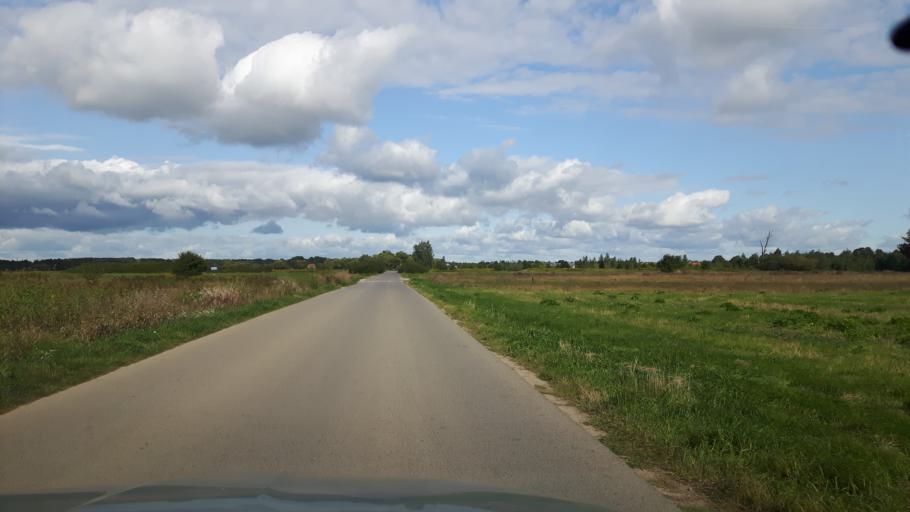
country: PL
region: Masovian Voivodeship
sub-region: Powiat wolominski
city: Marki
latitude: 52.3294
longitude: 21.0766
